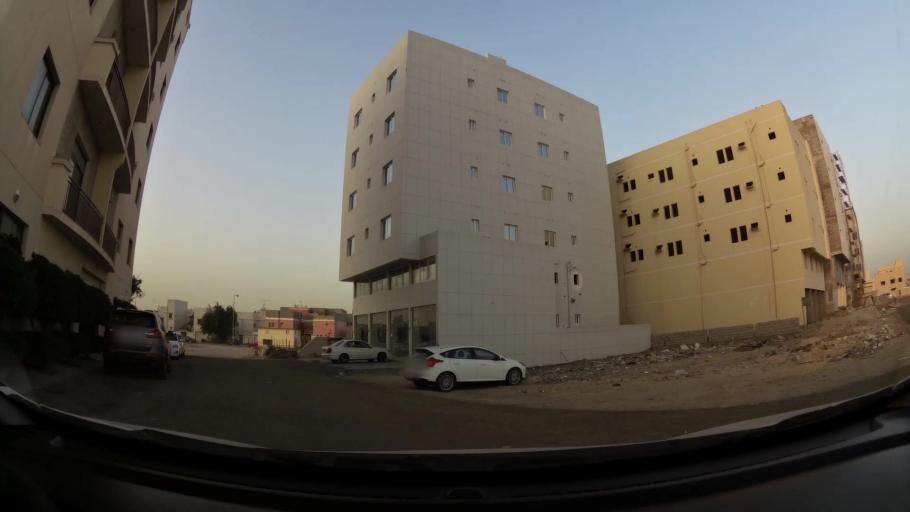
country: BH
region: Northern
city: Madinat `Isa
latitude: 26.1900
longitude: 50.4827
